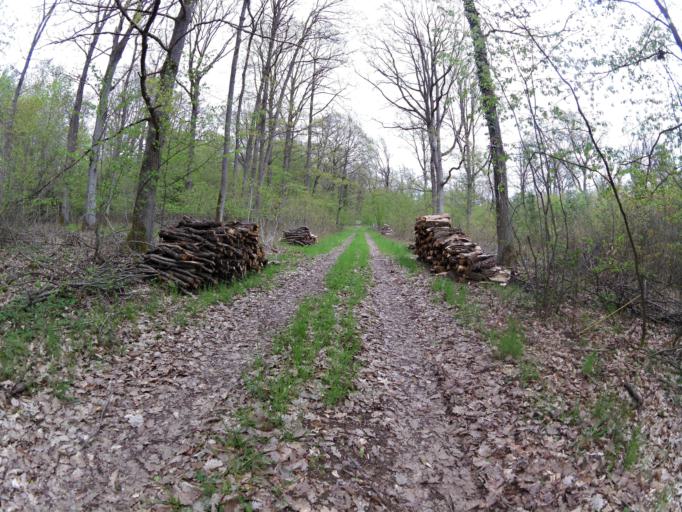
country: DE
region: Bavaria
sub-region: Regierungsbezirk Unterfranken
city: Prosselsheim
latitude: 49.8525
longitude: 10.1529
